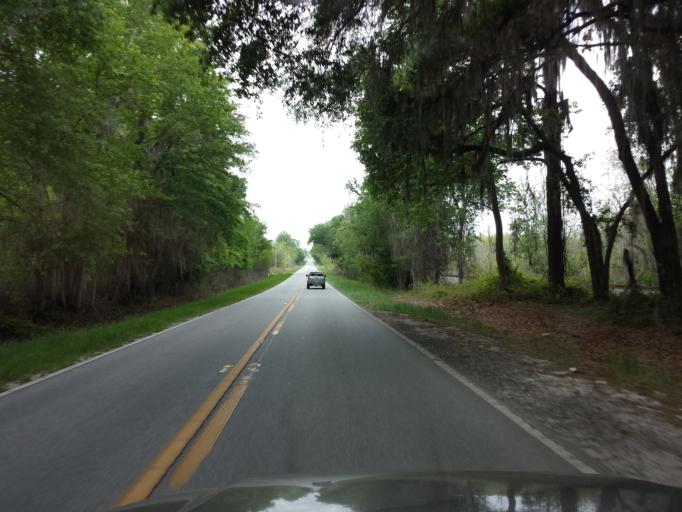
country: US
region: Georgia
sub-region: Echols County
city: Statenville
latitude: 30.6749
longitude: -83.1697
